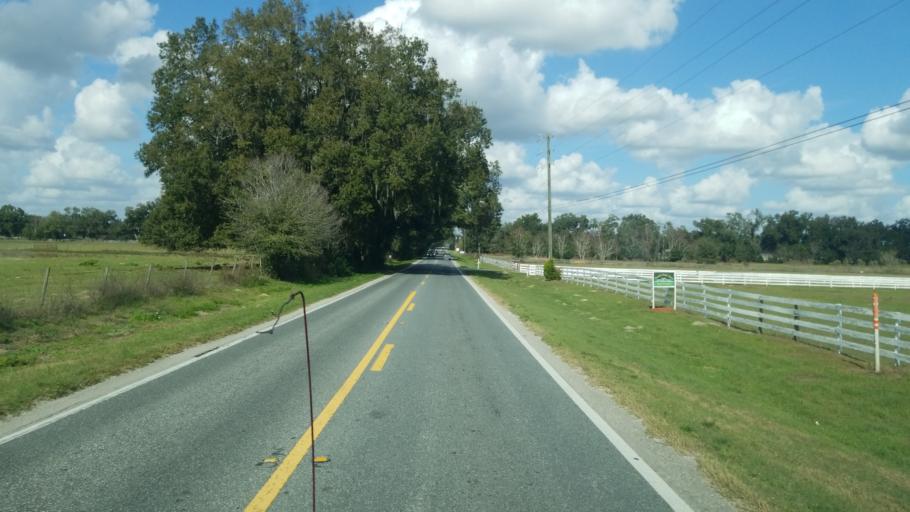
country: US
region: Florida
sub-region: Marion County
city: Belleview
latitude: 28.9858
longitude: -82.1199
